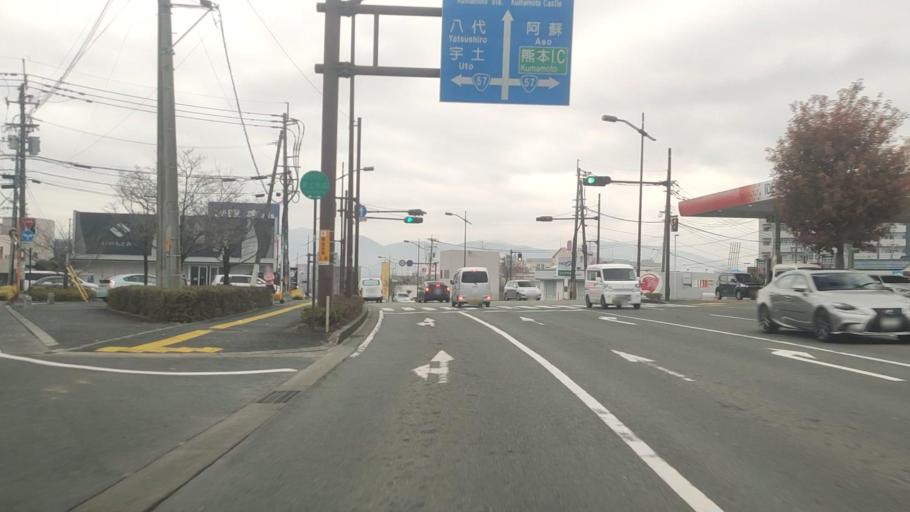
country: JP
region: Kumamoto
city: Kumamoto
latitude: 32.8071
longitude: 130.7506
